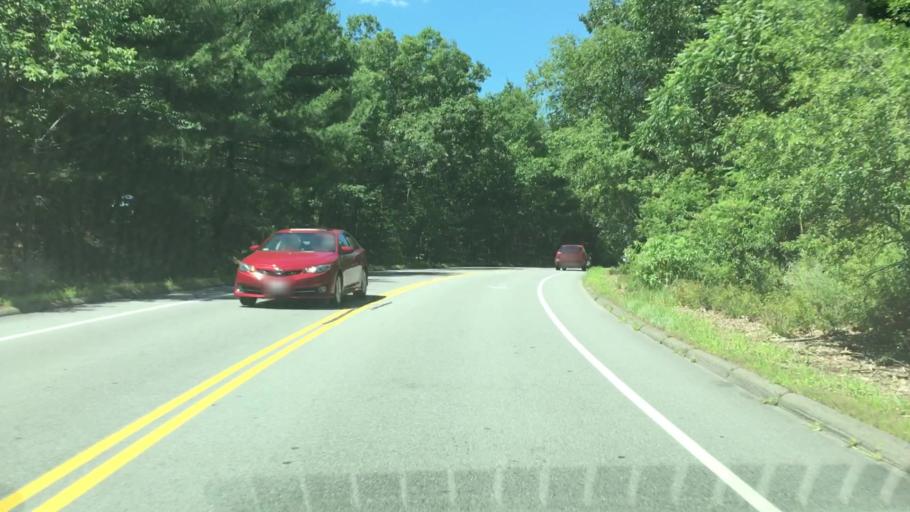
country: US
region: Massachusetts
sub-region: Middlesex County
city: Lexington
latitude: 42.4462
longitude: -71.2587
